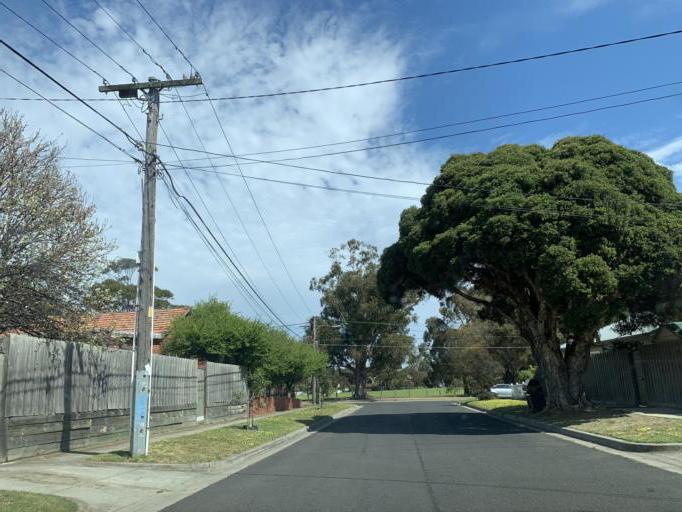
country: AU
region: Victoria
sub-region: Bayside
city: Hampton East
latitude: -37.9447
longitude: 145.0267
